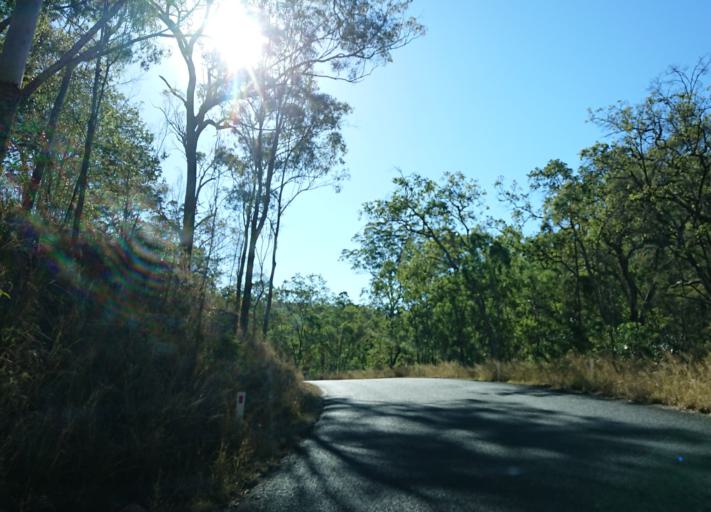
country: AU
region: Queensland
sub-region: Toowoomba
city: Top Camp
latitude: -27.7643
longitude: 152.0841
